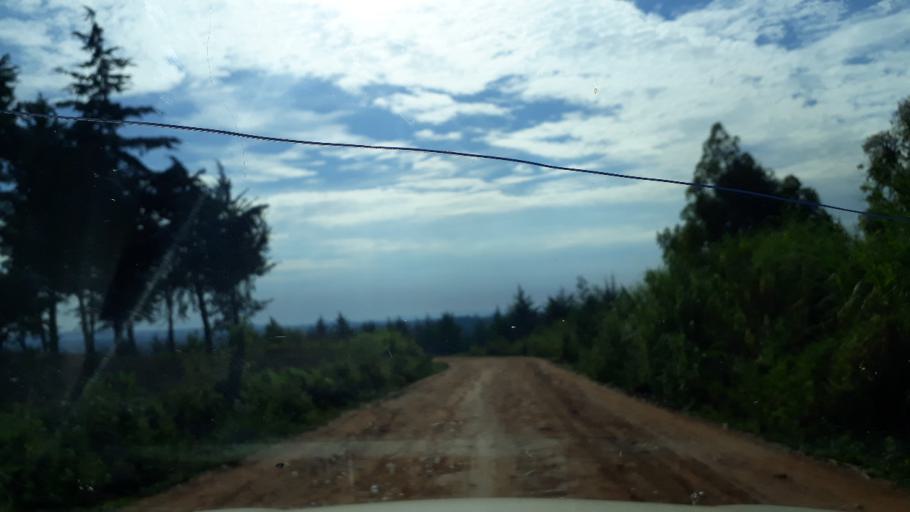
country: UG
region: Northern Region
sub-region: Zombo District
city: Paidha
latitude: 2.2846
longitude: 30.9693
